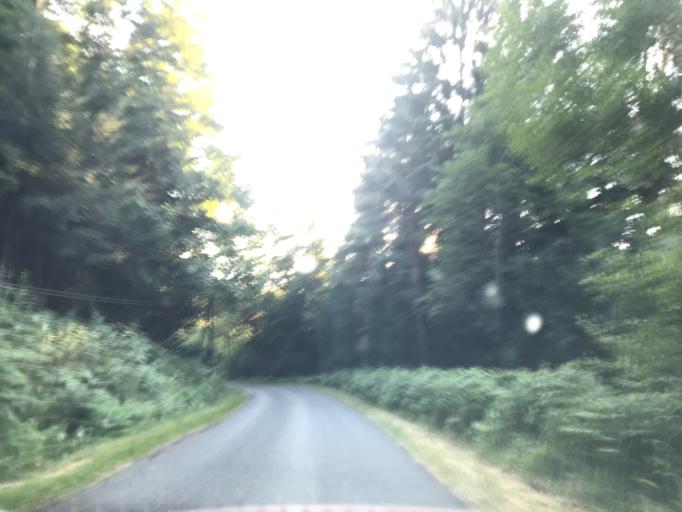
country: FR
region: Auvergne
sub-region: Departement du Puy-de-Dome
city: Courpiere
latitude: 45.7560
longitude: 3.6430
